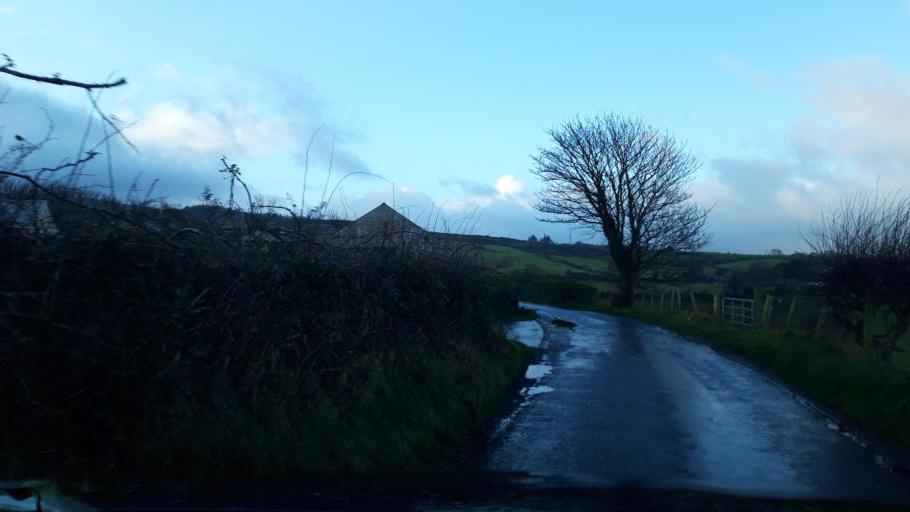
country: GB
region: Northern Ireland
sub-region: Moyle District
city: Ballycastle
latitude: 55.1973
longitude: -6.2228
